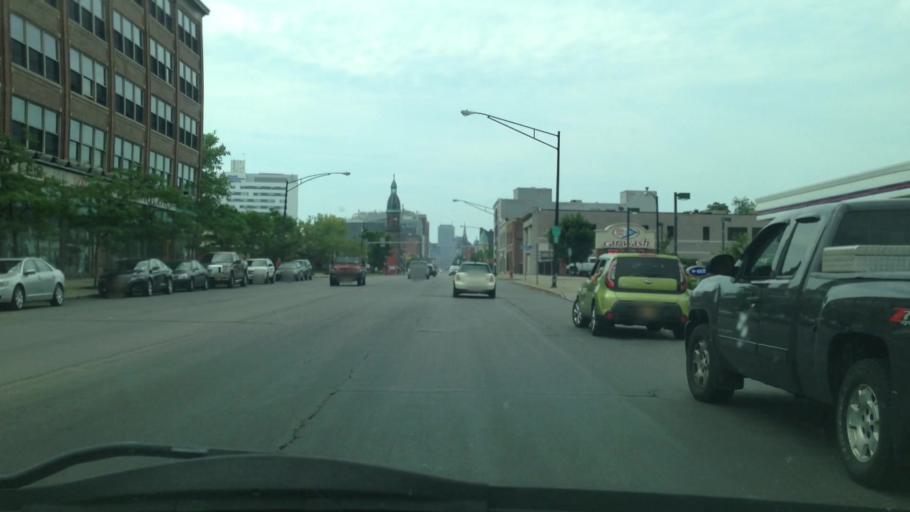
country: US
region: New York
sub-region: Erie County
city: Buffalo
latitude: 42.9074
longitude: -78.8673
